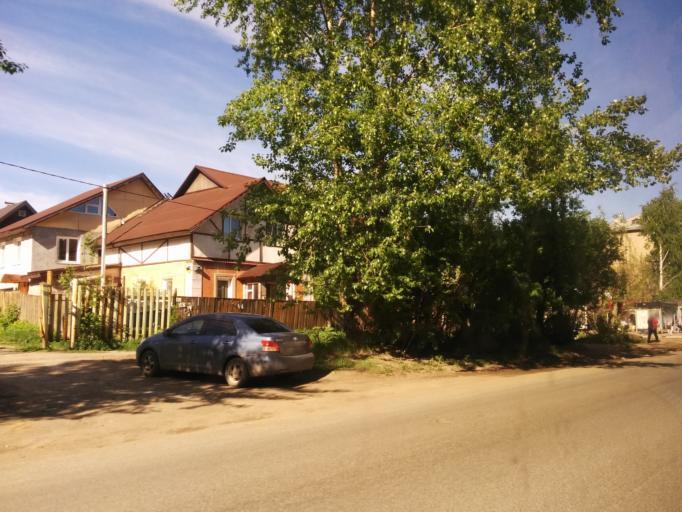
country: RU
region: Perm
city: Kondratovo
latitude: 58.0449
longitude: 56.0858
